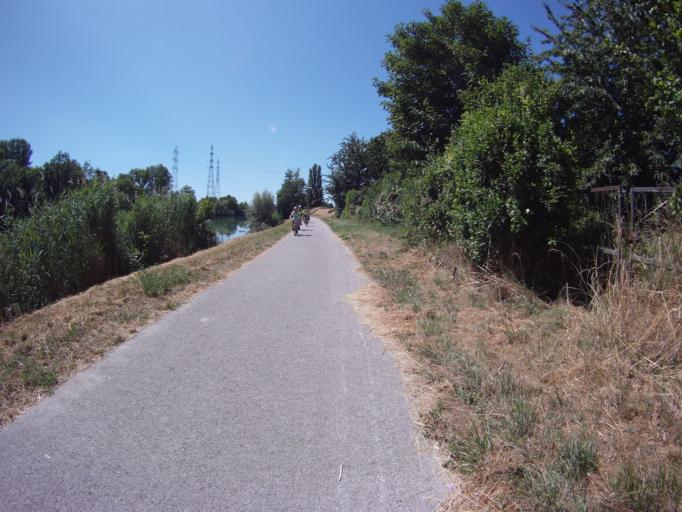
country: FR
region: Champagne-Ardenne
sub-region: Departement de la Marne
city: Damery
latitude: 49.0723
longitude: 3.8723
